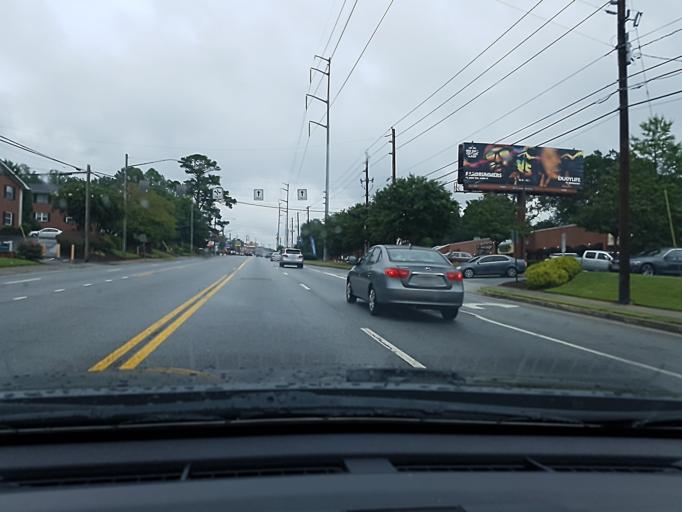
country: US
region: Georgia
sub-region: DeKalb County
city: North Atlanta
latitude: 33.8712
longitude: -84.3810
